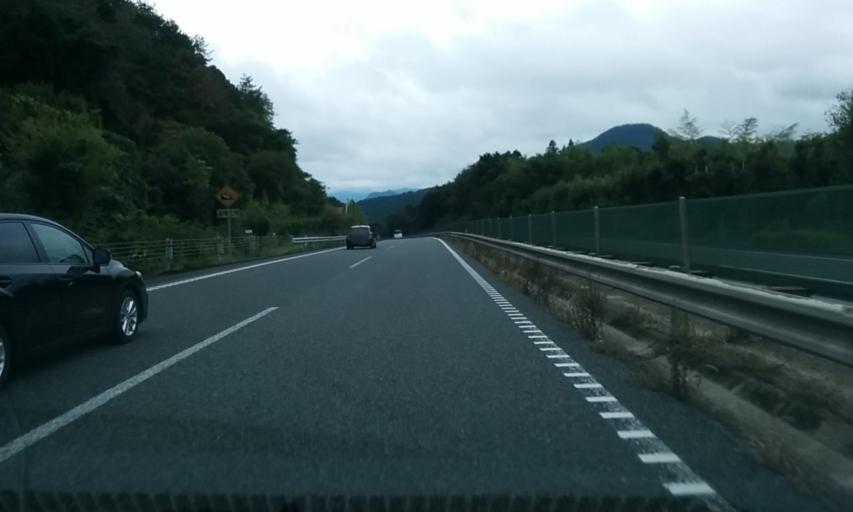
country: JP
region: Kyoto
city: Fukuchiyama
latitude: 35.1757
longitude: 135.1295
